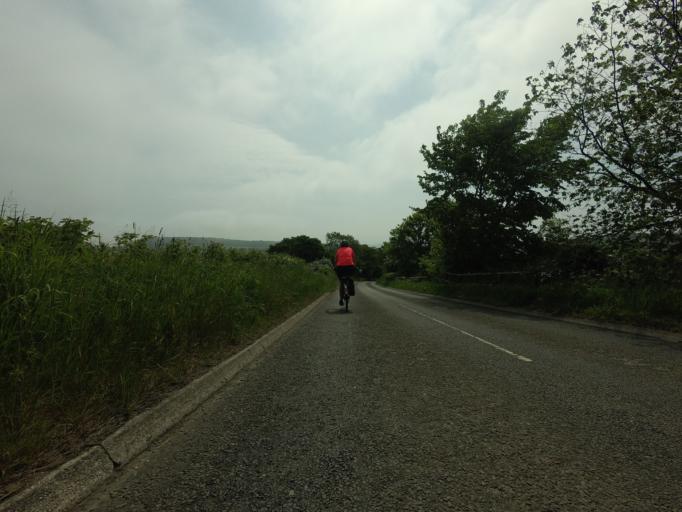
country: GB
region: Scotland
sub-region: Fife
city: Inverkeithing
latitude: 56.0458
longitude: -3.3980
